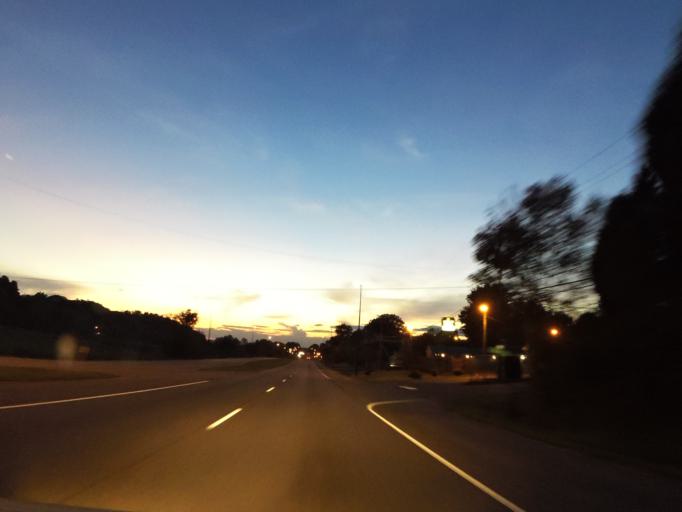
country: US
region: Tennessee
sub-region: Knox County
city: Mascot
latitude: 36.0196
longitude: -83.7980
